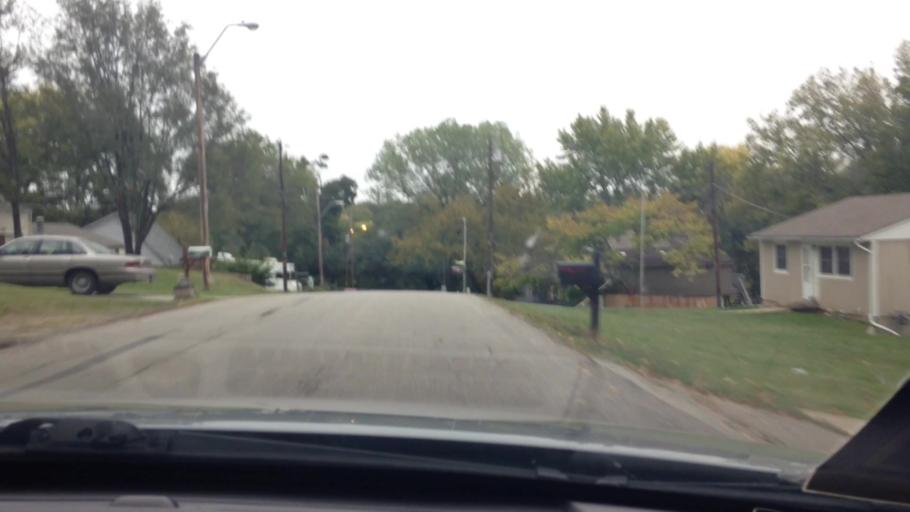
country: US
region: Missouri
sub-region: Clay County
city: North Kansas City
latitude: 39.1622
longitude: -94.5507
